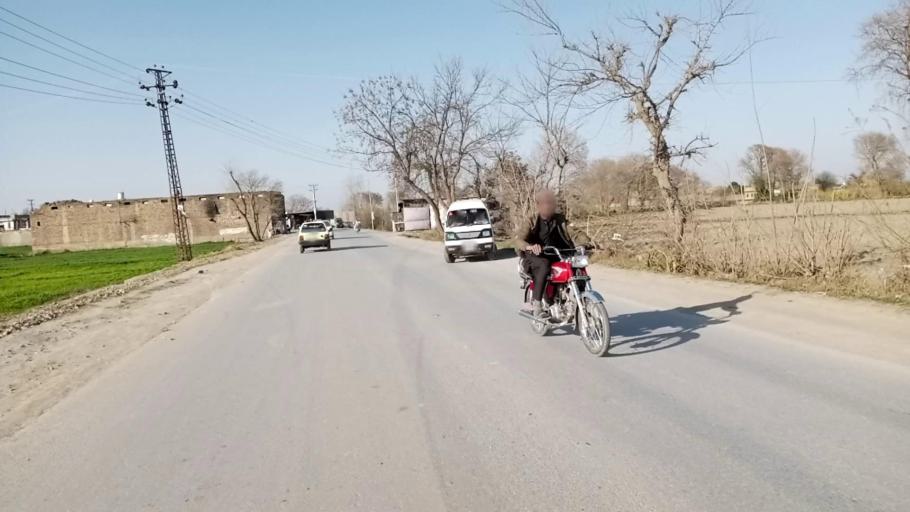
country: PK
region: Khyber Pakhtunkhwa
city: Peshawar
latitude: 34.0869
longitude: 71.5306
